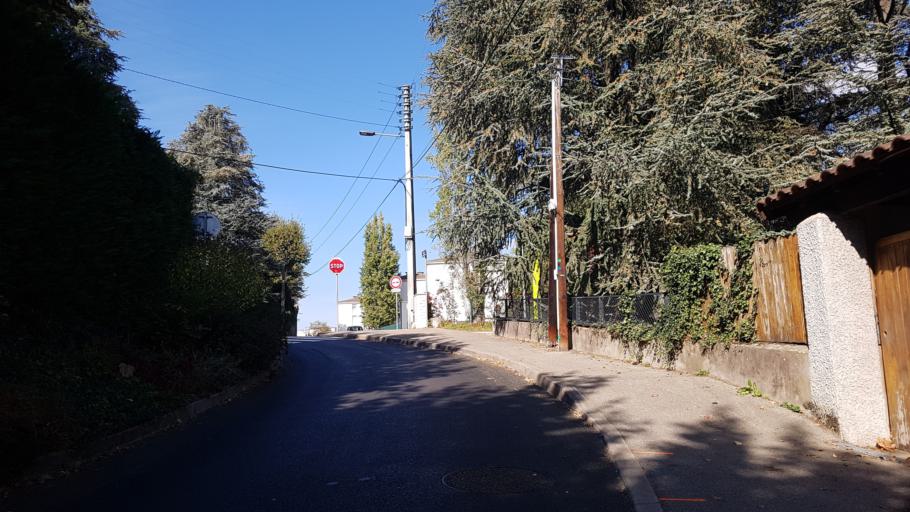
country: FR
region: Rhone-Alpes
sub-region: Departement du Rhone
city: Ecully
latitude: 45.7812
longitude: 4.7900
